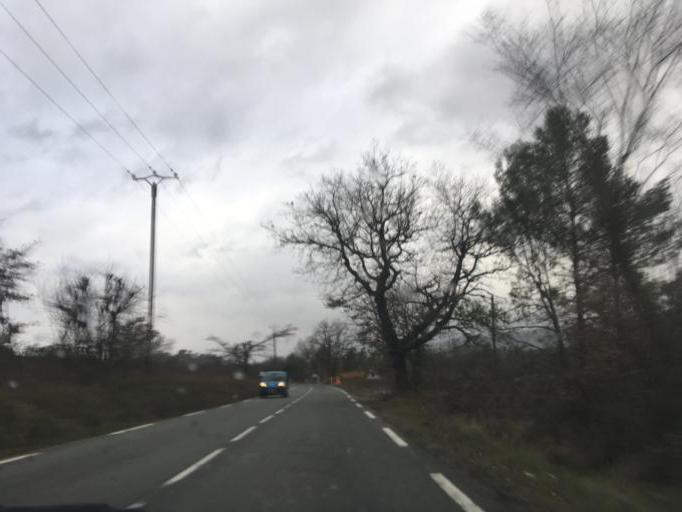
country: FR
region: Provence-Alpes-Cote d'Azur
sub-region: Departement du Var
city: Sainte-Anastasie-sur-Issole
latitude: 43.3389
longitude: 6.1149
